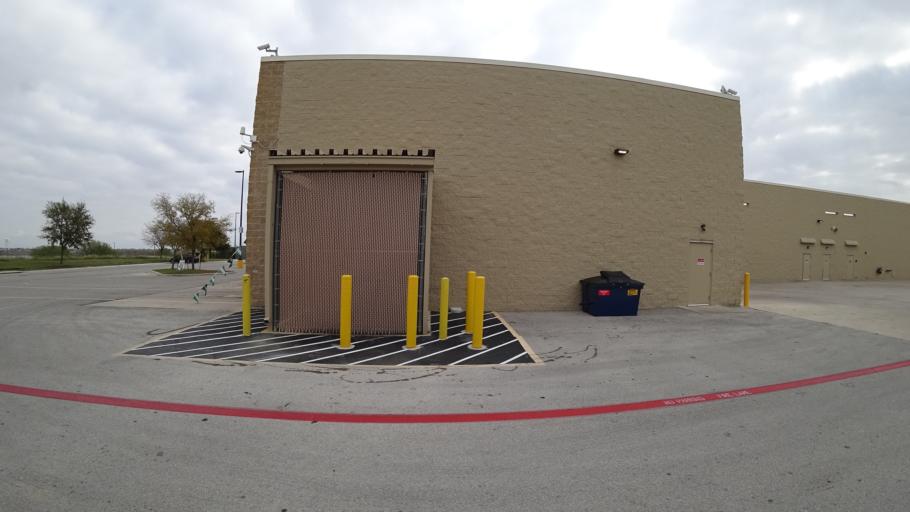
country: US
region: Texas
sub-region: Travis County
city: Pflugerville
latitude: 30.4546
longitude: -97.6072
